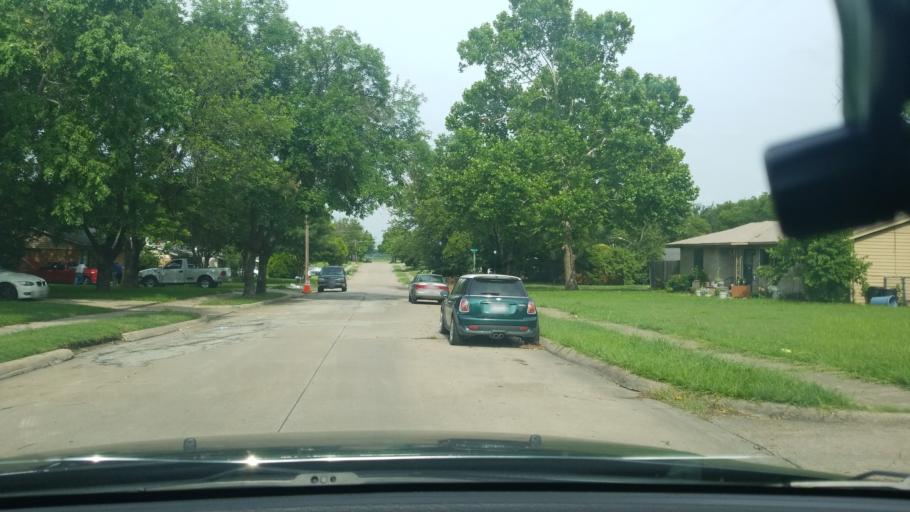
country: US
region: Texas
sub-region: Dallas County
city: Mesquite
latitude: 32.7600
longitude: -96.6256
